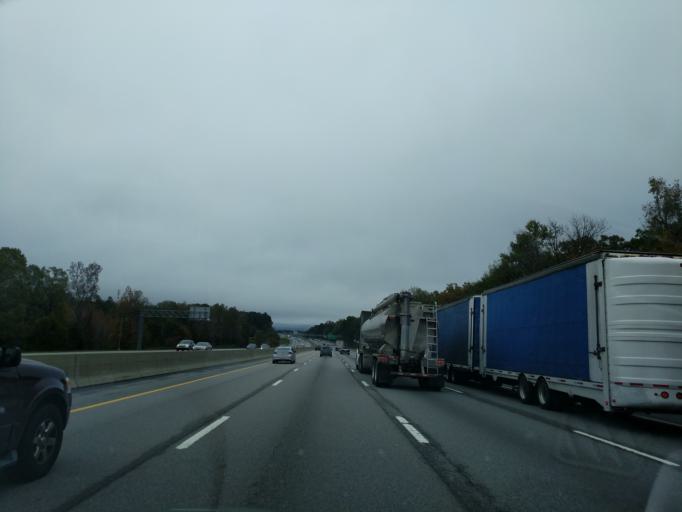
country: US
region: North Carolina
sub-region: Alamance County
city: Mebane
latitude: 36.0747
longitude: -79.1885
